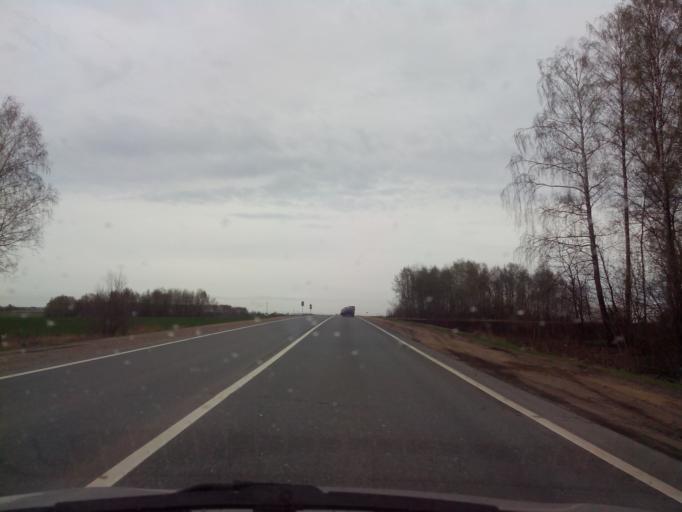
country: RU
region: Moskovskaya
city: Kashira
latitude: 54.7709
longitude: 38.1693
